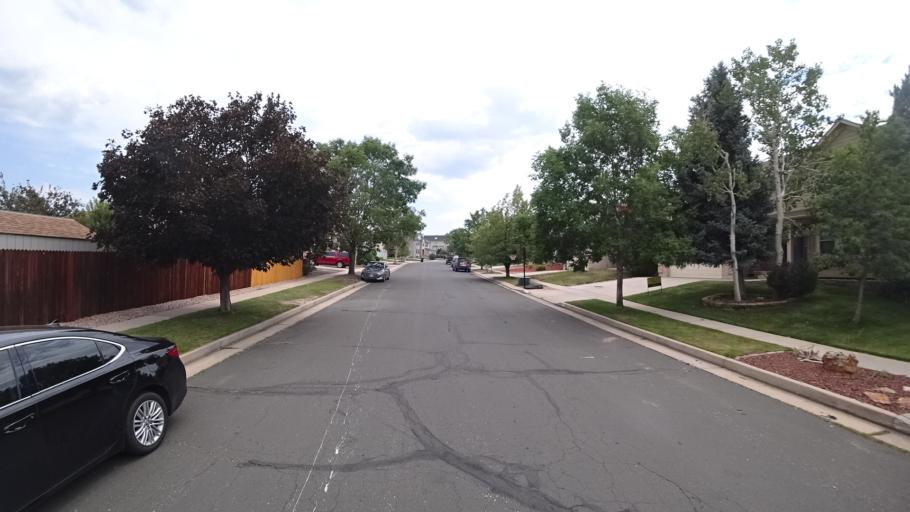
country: US
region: Colorado
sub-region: El Paso County
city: Black Forest
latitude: 38.9597
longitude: -104.7766
